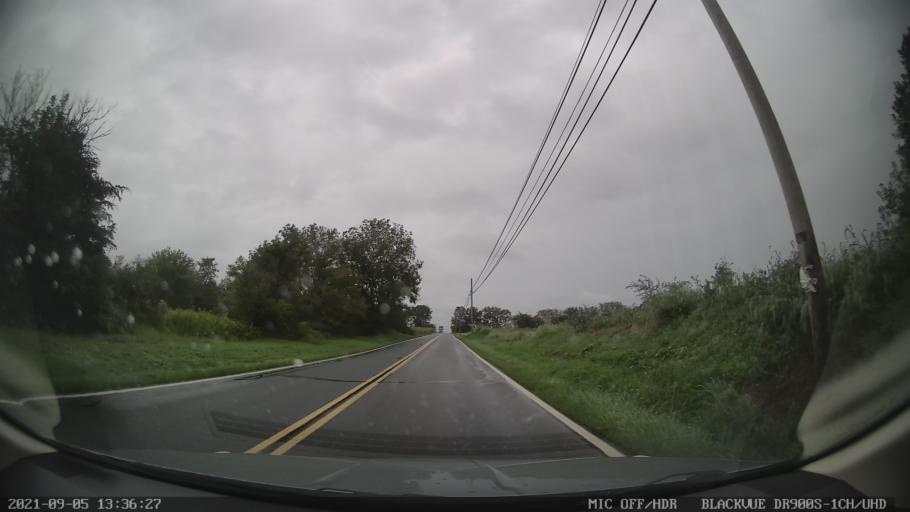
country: US
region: Pennsylvania
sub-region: Lehigh County
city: Breinigsville
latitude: 40.5784
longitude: -75.6561
